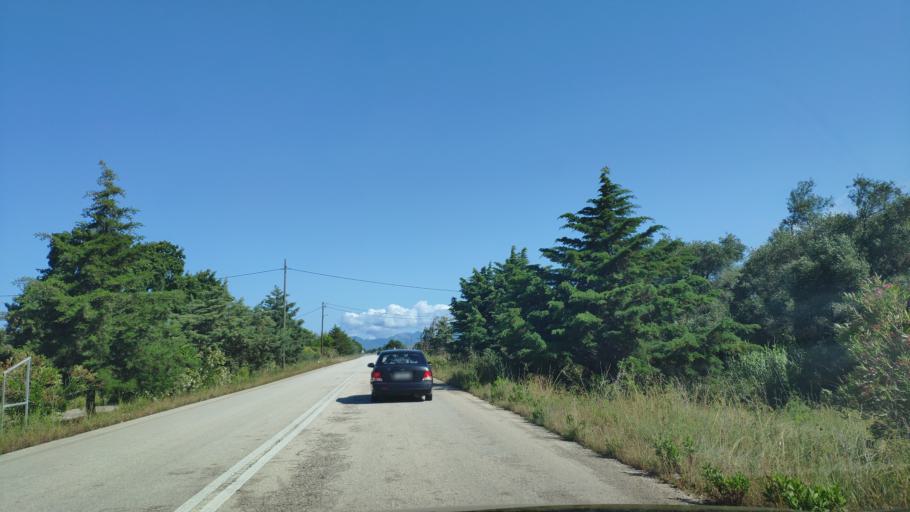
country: GR
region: Epirus
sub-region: Nomos Prevezis
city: Preveza
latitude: 38.9680
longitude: 20.7242
